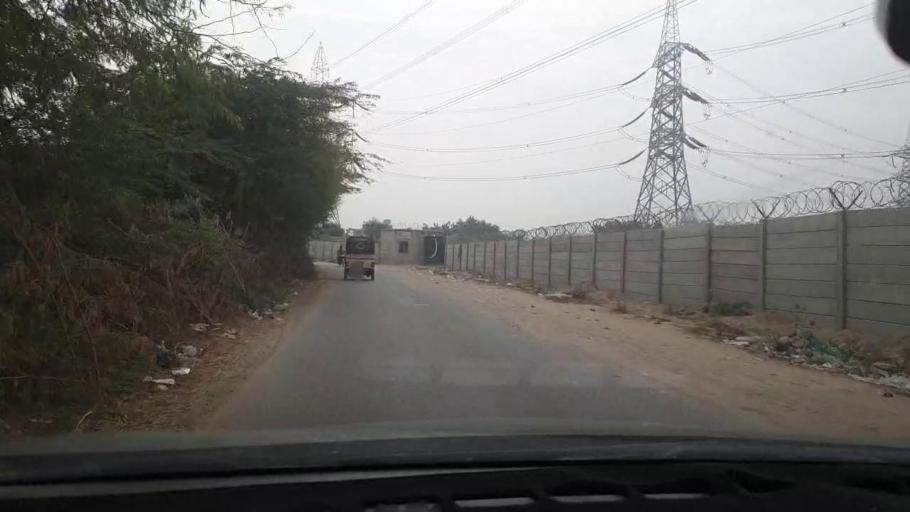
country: PK
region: Sindh
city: Malir Cantonment
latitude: 24.9092
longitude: 67.2855
